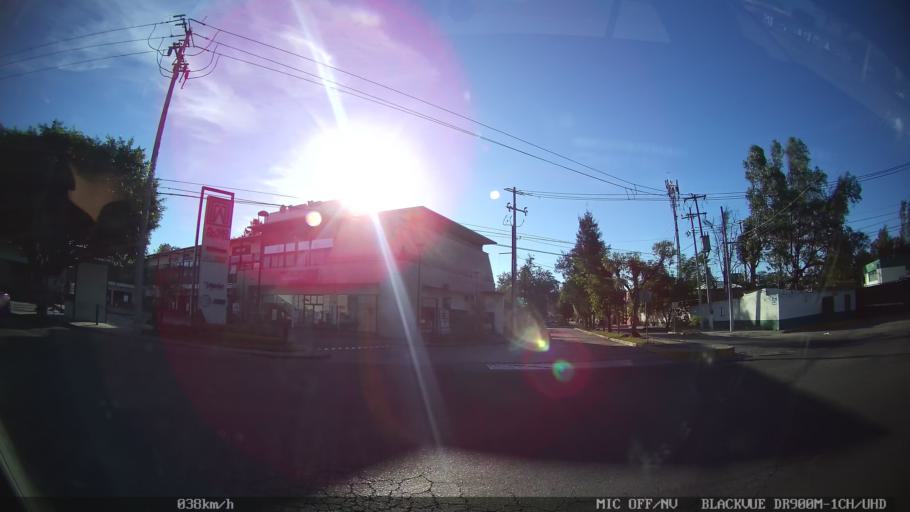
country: MX
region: Jalisco
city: Tlaquepaque
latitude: 20.6256
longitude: -103.3208
